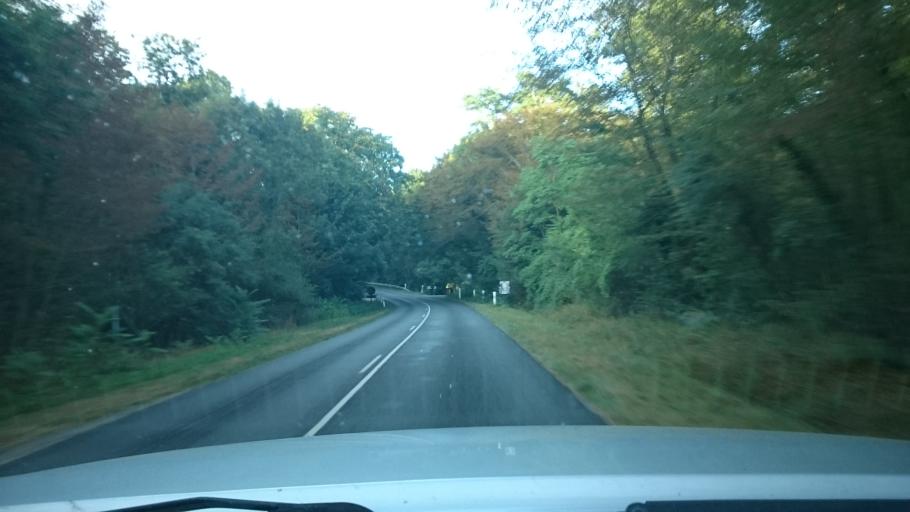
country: FR
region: Ile-de-France
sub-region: Departement de Seine-et-Marne
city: Samois-sur-Seine
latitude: 48.4836
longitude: 2.7504
